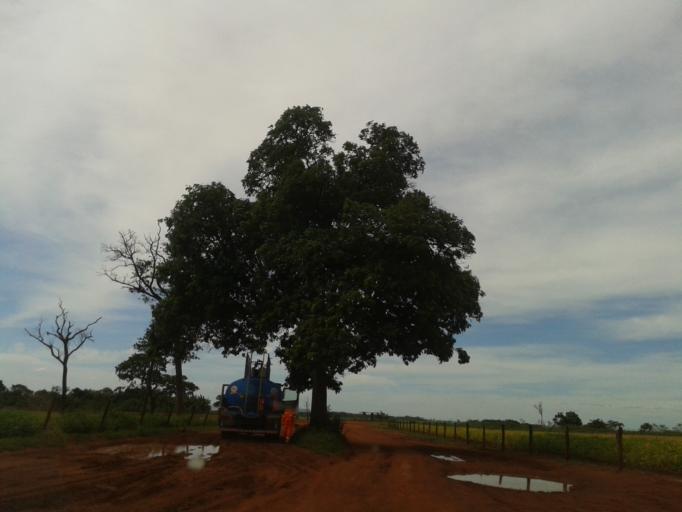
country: BR
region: Minas Gerais
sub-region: Capinopolis
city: Capinopolis
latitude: -18.7134
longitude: -49.8430
